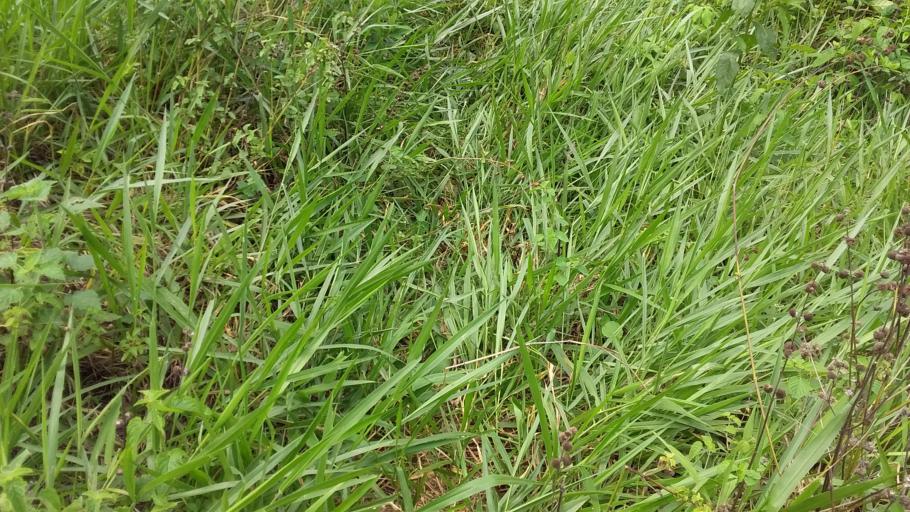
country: CO
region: Casanare
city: Nunchia
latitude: 5.6107
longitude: -72.2939
